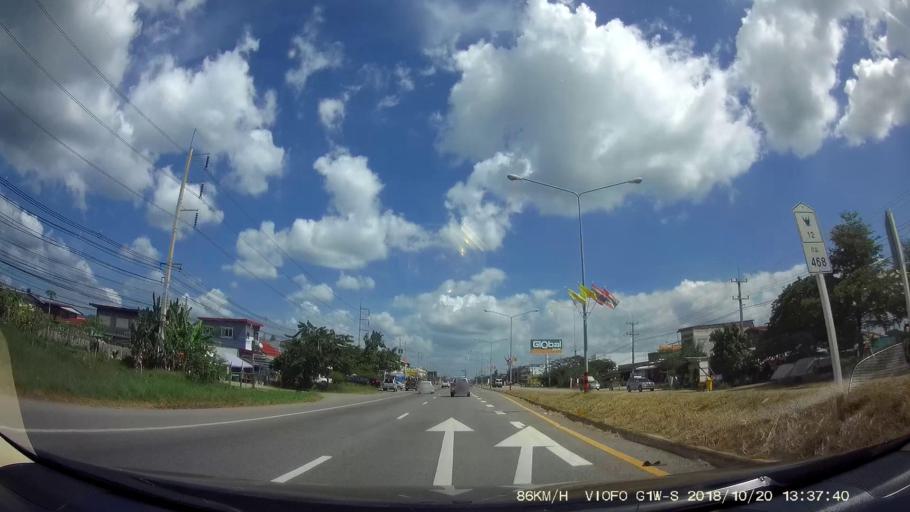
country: TH
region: Khon Kaen
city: Chum Phae
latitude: 16.5567
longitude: 102.0738
